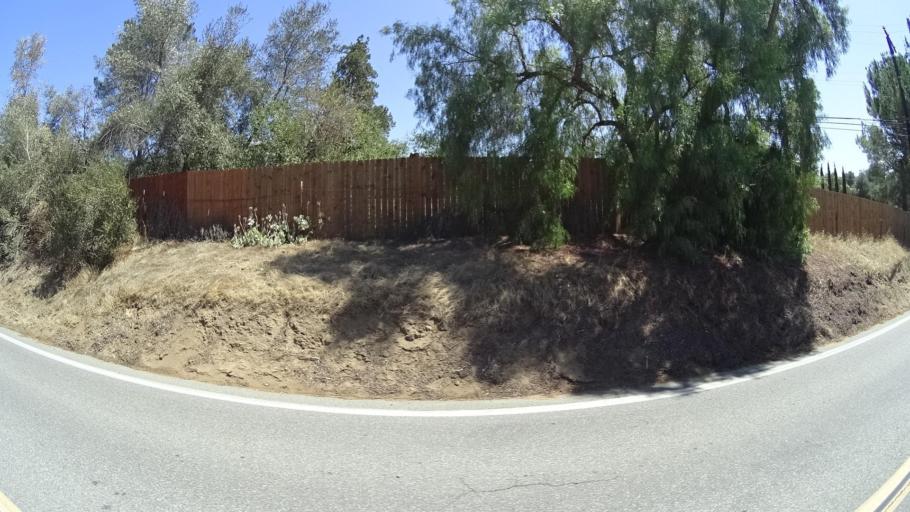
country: US
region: California
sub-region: San Diego County
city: Fallbrook
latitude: 33.3609
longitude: -117.2038
